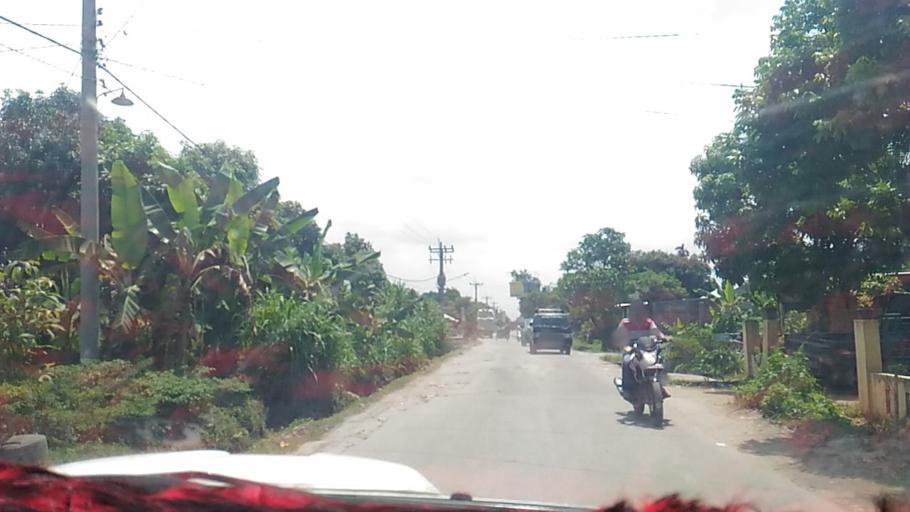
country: ID
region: North Sumatra
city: Sunggal
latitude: 3.5232
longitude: 98.5497
